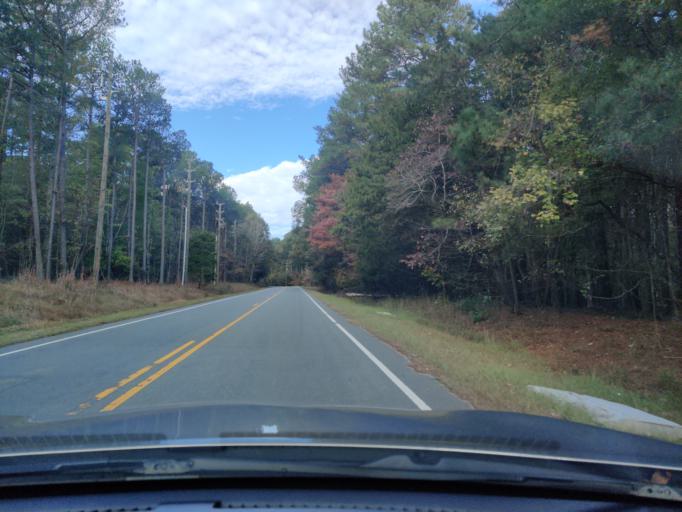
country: US
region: North Carolina
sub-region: Wake County
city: West Raleigh
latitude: 35.9199
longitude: -78.7172
